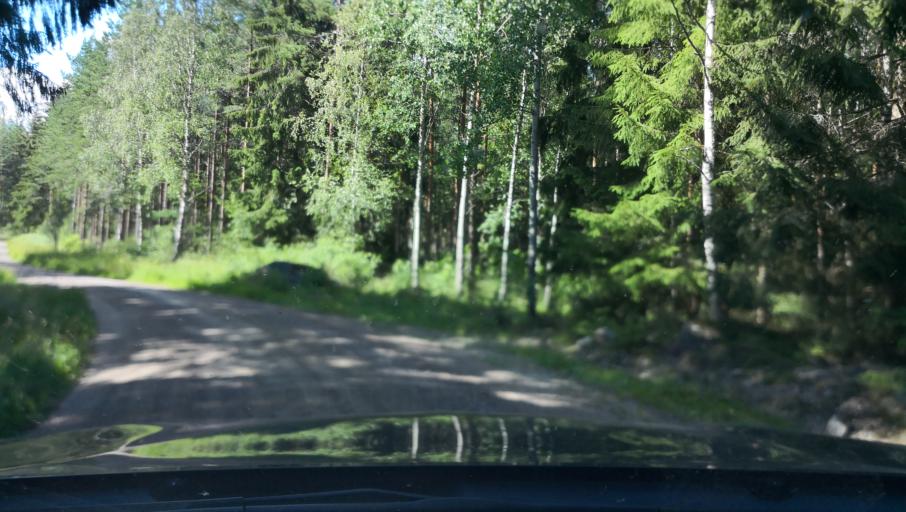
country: SE
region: Vaestmanland
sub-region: Kungsors Kommun
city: Kungsoer
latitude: 59.3259
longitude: 16.0438
